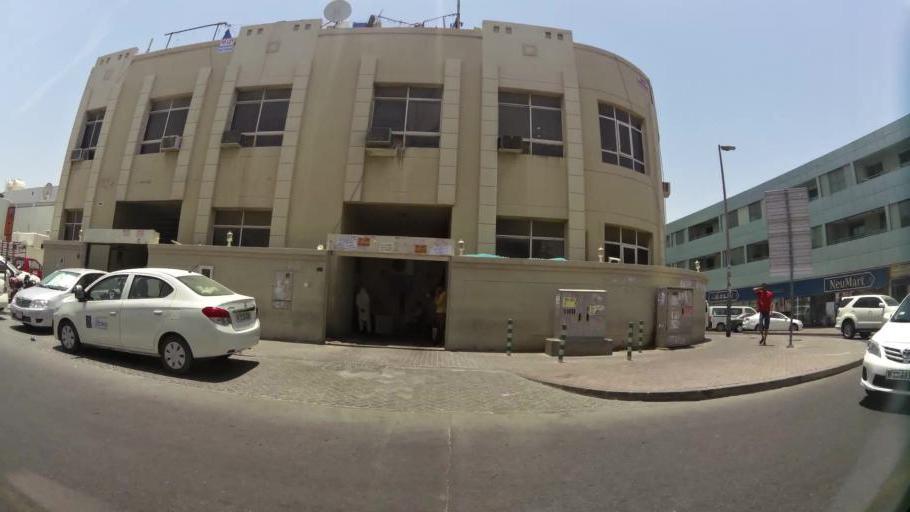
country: AE
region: Ash Shariqah
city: Sharjah
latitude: 25.2762
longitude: 55.3360
